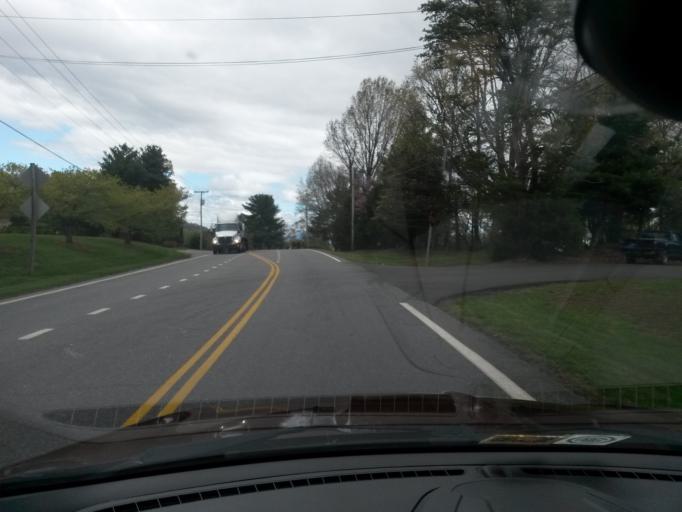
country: US
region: Virginia
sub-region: Bedford County
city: Forest
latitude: 37.4531
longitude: -79.2616
